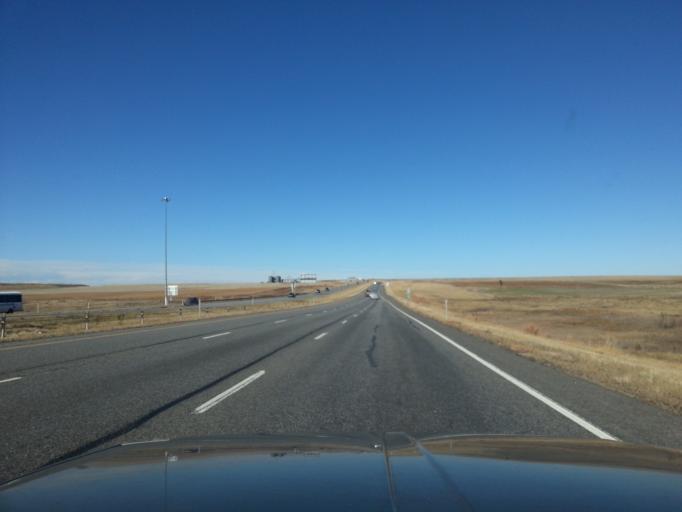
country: US
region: Colorado
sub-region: Adams County
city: Aurora
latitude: 39.8420
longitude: -104.7467
